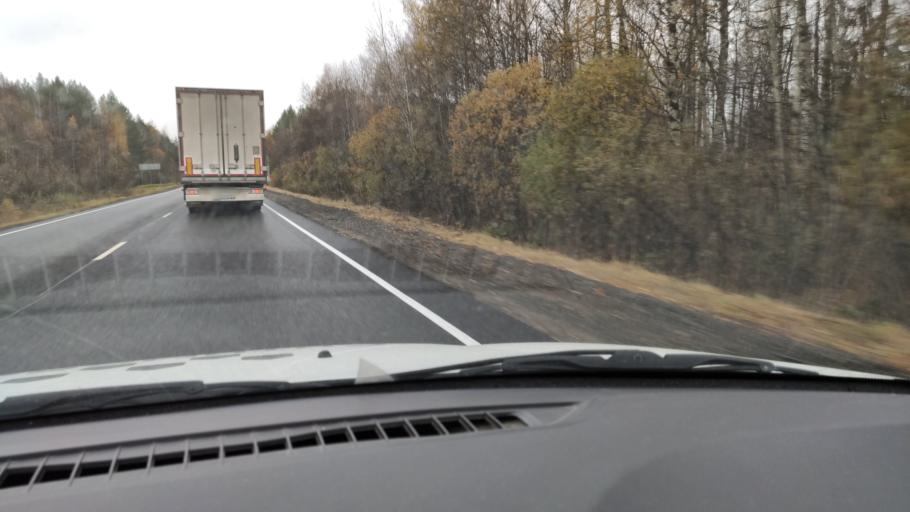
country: RU
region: Kirov
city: Slobodskoy
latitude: 58.7259
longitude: 50.2120
